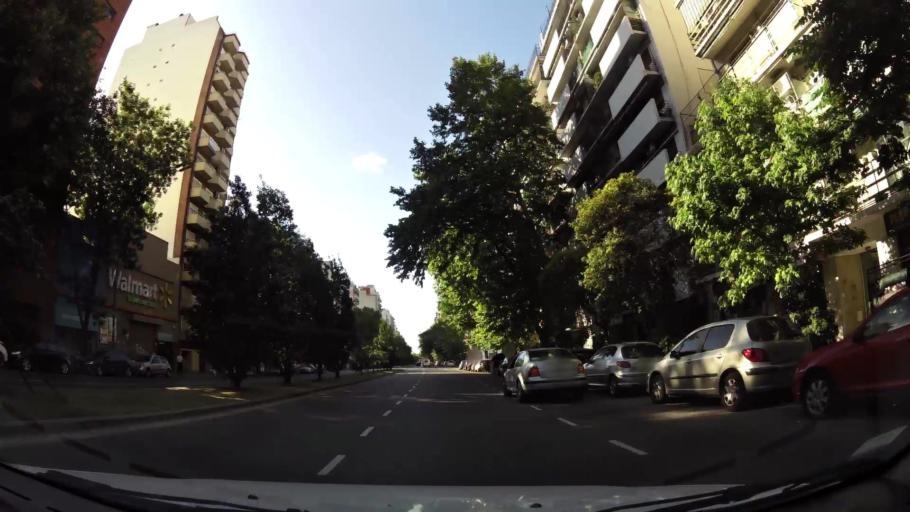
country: AR
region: Buenos Aires F.D.
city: Villa Santa Rita
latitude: -34.6125
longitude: -58.4417
